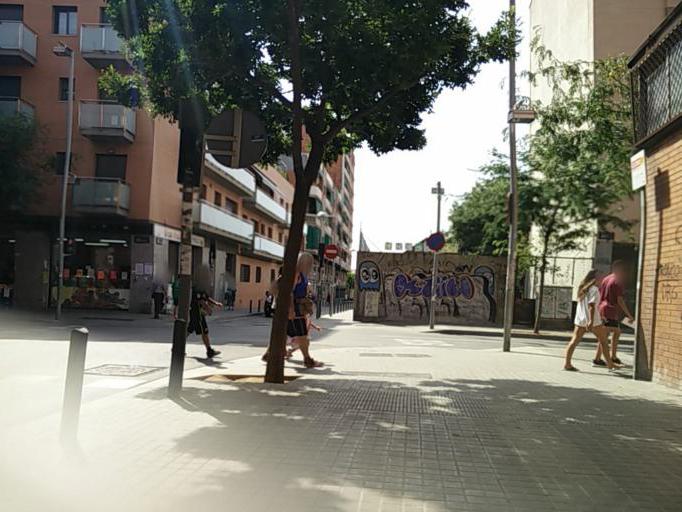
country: ES
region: Catalonia
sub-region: Provincia de Barcelona
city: Badalona
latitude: 41.4455
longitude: 2.2372
